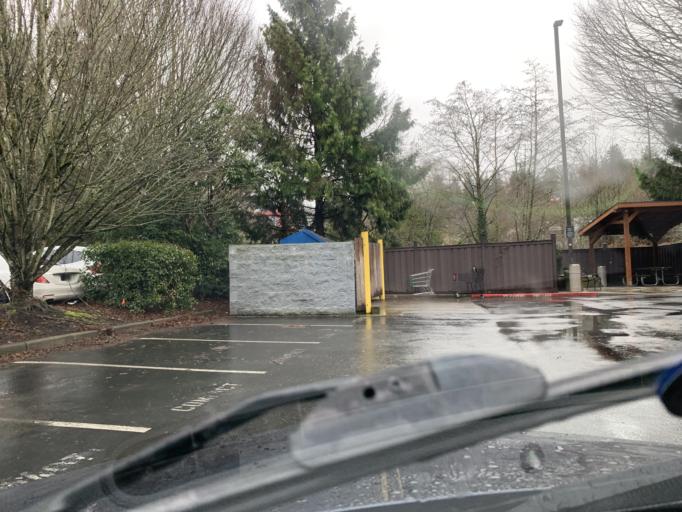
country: US
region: Washington
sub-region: King County
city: Bellevue
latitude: 47.6111
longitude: -122.1877
